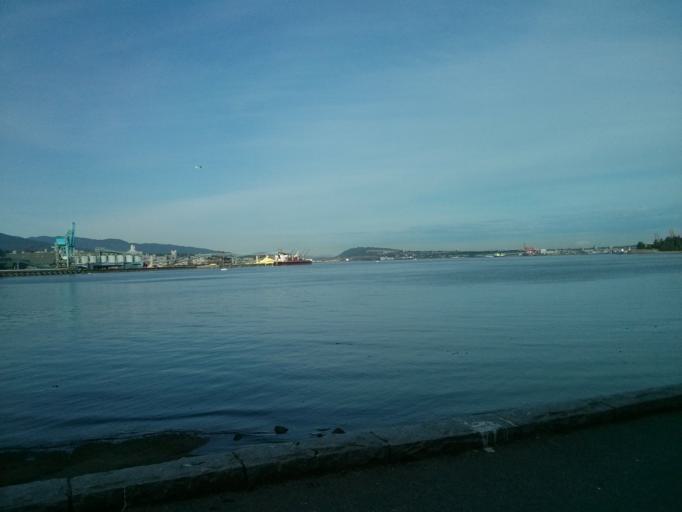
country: CA
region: British Columbia
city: West End
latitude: 49.3097
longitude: -123.1366
